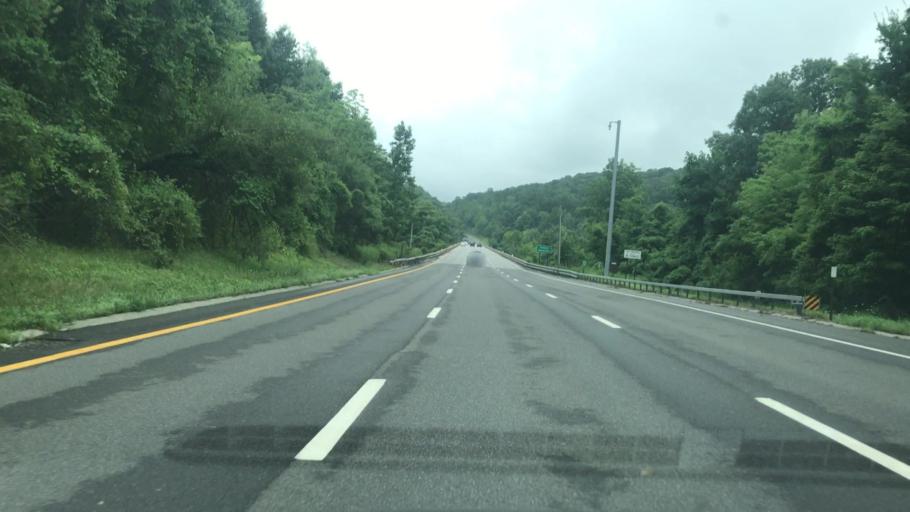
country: US
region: New York
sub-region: Westchester County
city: Yorktown Heights
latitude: 41.2422
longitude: -73.8169
